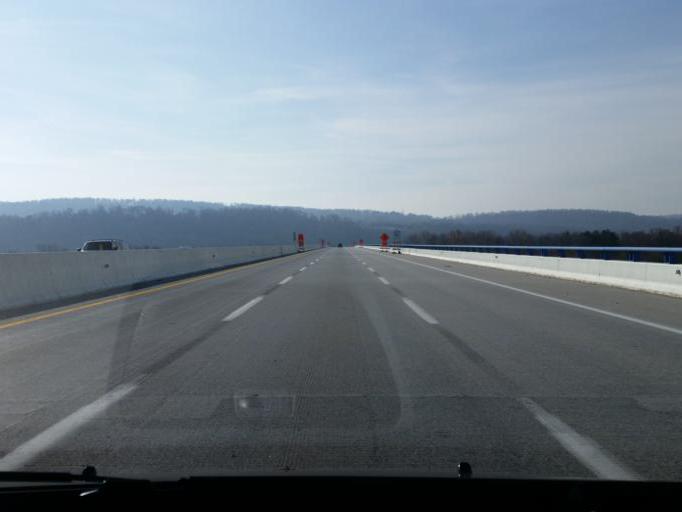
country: US
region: Pennsylvania
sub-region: Dauphin County
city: Highspire
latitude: 40.2084
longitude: -76.8015
